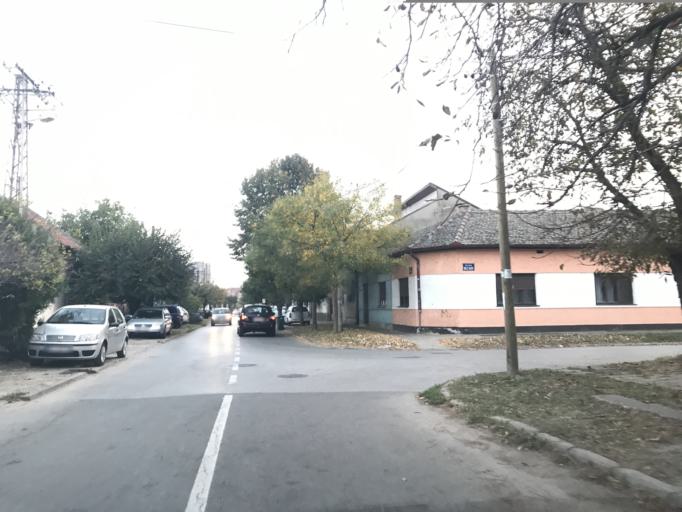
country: RS
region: Autonomna Pokrajina Vojvodina
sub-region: Juznobacki Okrug
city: Novi Sad
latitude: 45.2660
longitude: 19.8495
